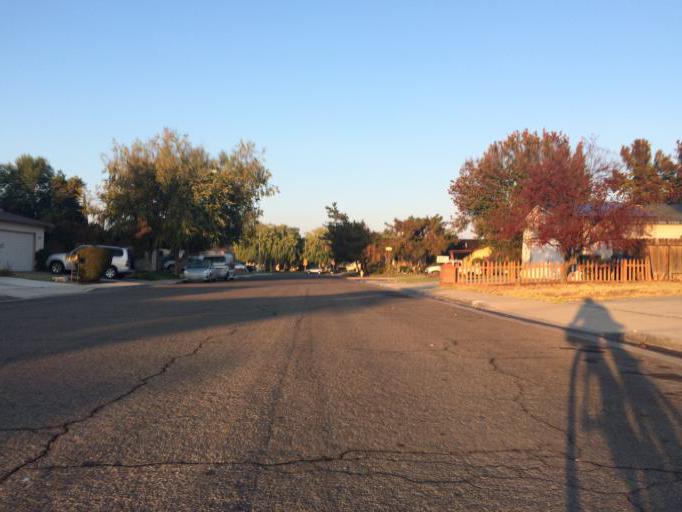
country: US
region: California
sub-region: Fresno County
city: Tarpey Village
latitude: 36.8046
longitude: -119.6849
